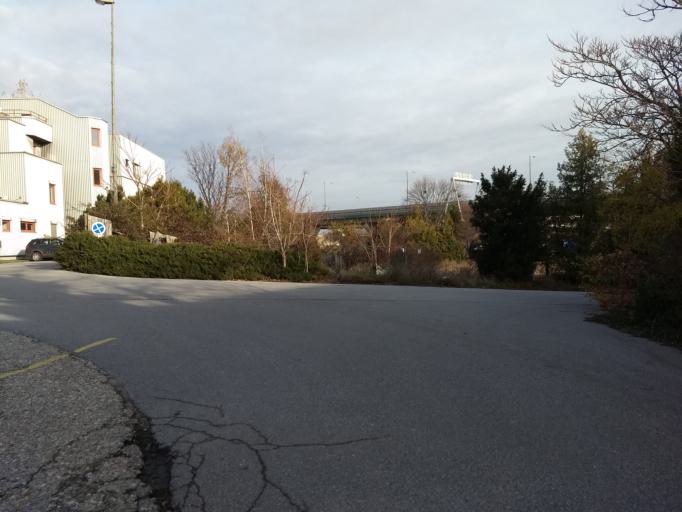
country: AT
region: Vienna
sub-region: Wien Stadt
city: Vienna
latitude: 48.2534
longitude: 16.3691
